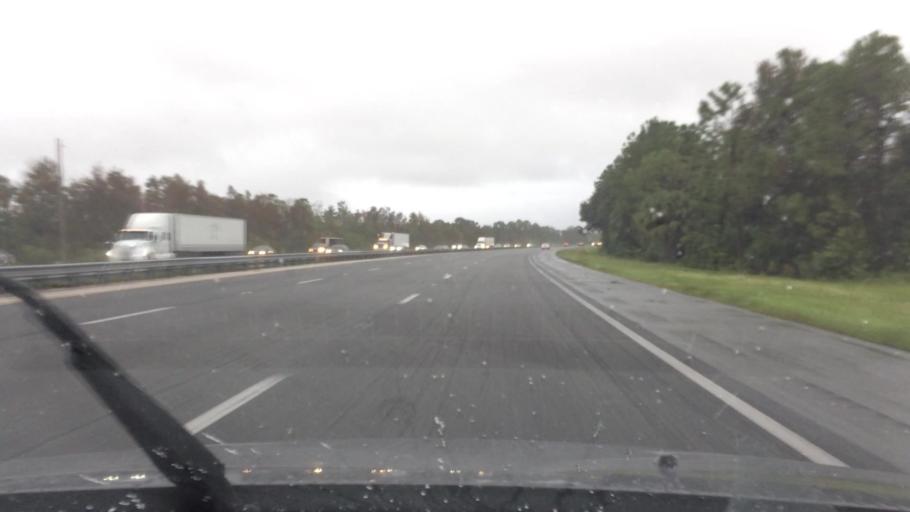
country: US
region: Florida
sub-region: Volusia County
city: Ormond Beach
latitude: 29.3014
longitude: -81.1313
